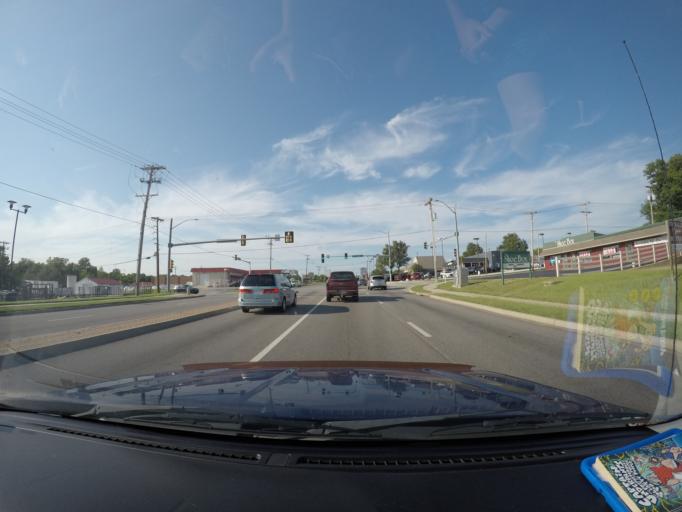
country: US
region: Kansas
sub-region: Leavenworth County
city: Lansing
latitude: 39.2666
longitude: -94.8998
